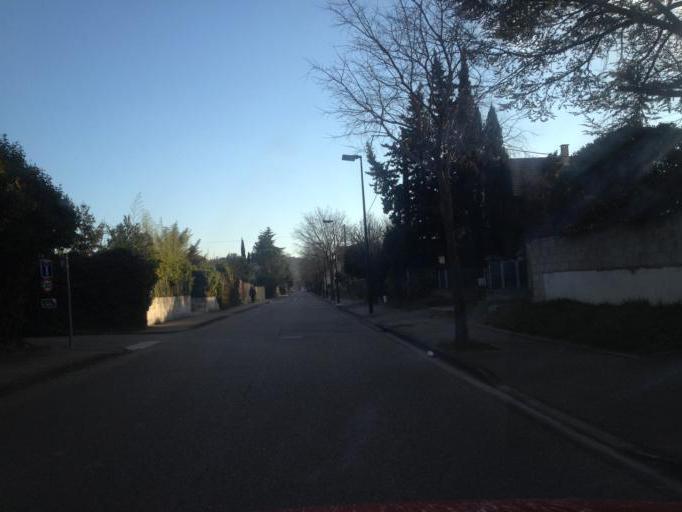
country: FR
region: Provence-Alpes-Cote d'Azur
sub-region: Departement du Vaucluse
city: Orange
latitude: 44.1455
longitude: 4.8085
